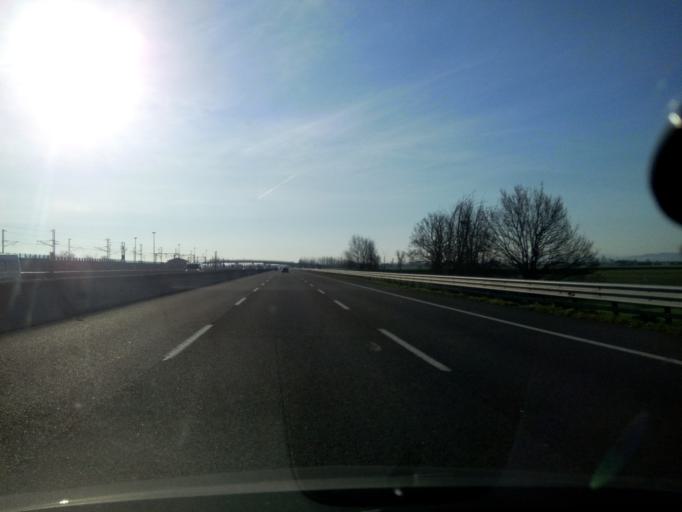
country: IT
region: Emilia-Romagna
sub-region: Provincia di Reggio Emilia
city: Campegine
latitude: 44.7613
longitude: 10.5339
